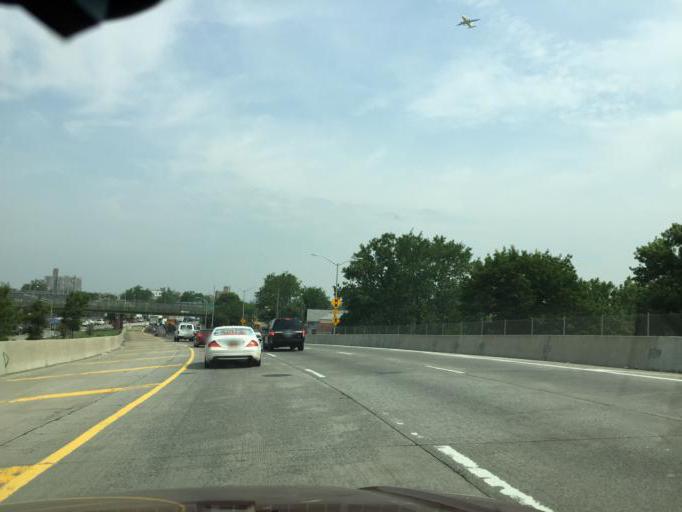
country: US
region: New York
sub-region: Bronx
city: The Bronx
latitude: 40.8368
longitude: -73.8246
